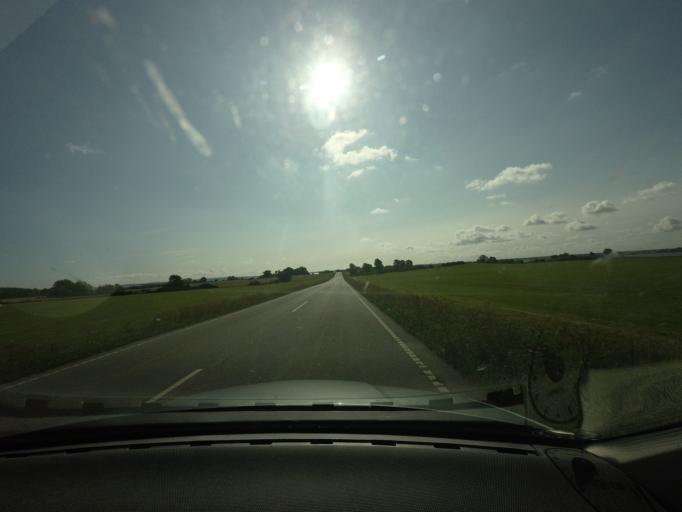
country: DK
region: Zealand
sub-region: Vordingborg Kommune
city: Stege
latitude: 55.0049
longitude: 12.1479
